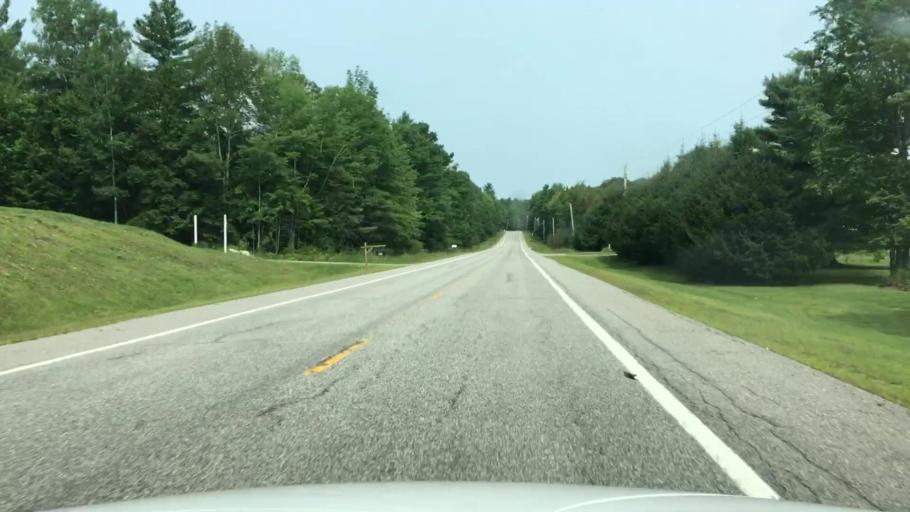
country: US
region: Maine
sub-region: Kennebec County
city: Wayne
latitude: 44.3646
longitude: -70.0883
